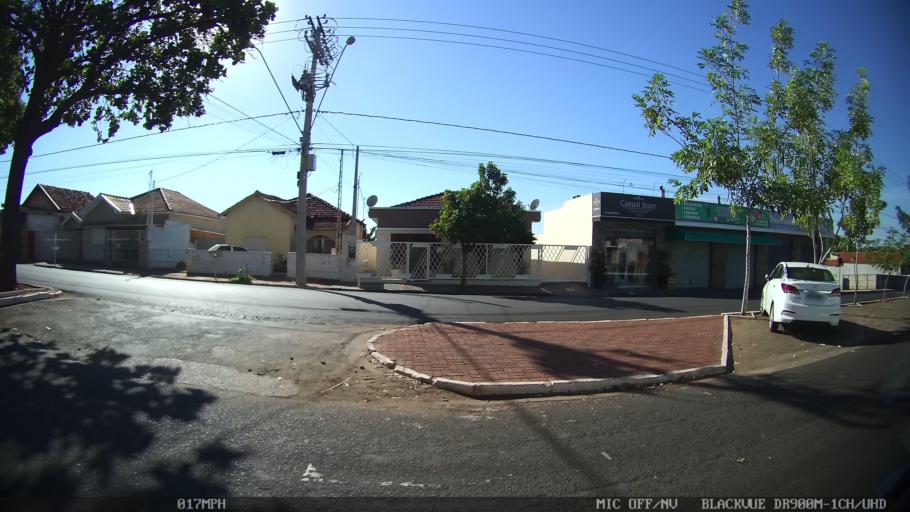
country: BR
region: Sao Paulo
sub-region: Olimpia
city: Olimpia
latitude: -20.7450
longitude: -48.9101
